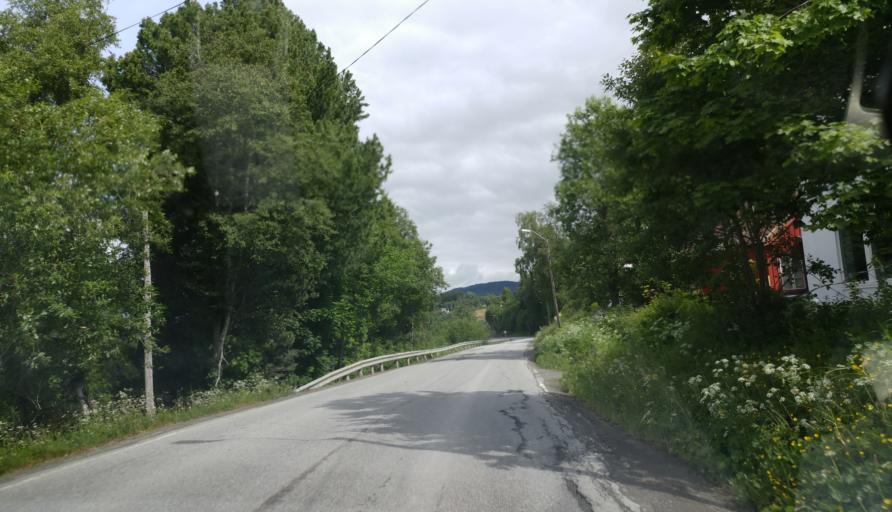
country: NO
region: Sor-Trondelag
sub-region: Selbu
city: Mebonden
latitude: 63.2360
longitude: 11.0408
